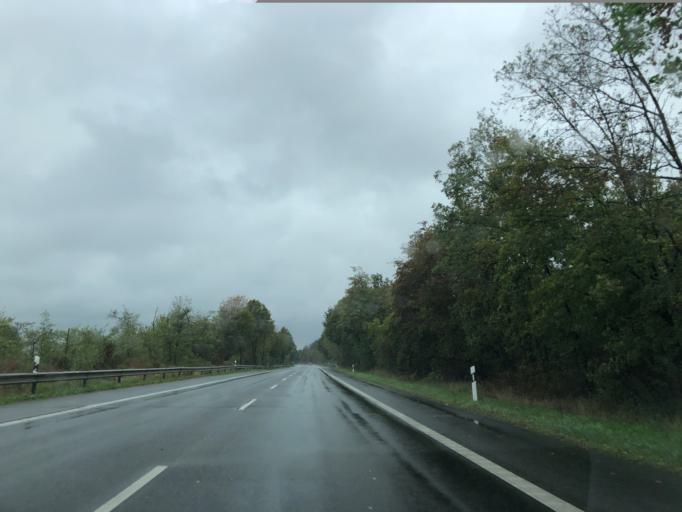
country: DE
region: North Rhine-Westphalia
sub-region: Regierungsbezirk Dusseldorf
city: Grevenbroich
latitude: 51.0733
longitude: 6.5579
